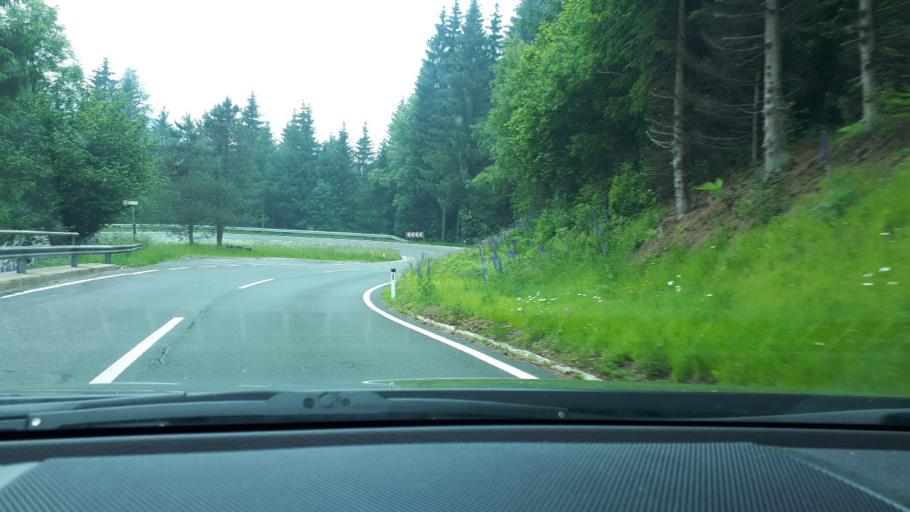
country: AT
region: Carinthia
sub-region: Politischer Bezirk Wolfsberg
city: Preitenegg
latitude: 46.9314
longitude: 14.8908
